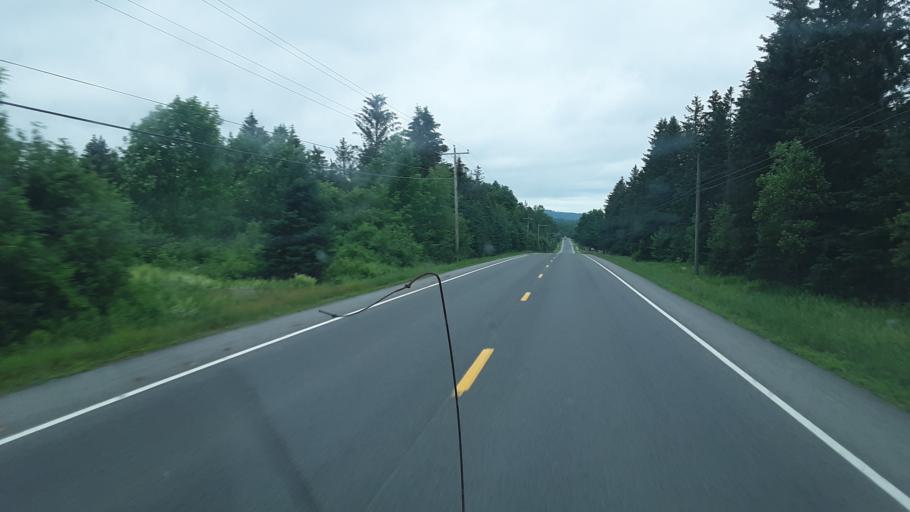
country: US
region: Maine
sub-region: Penobscot County
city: Patten
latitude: 45.9401
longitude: -68.4512
